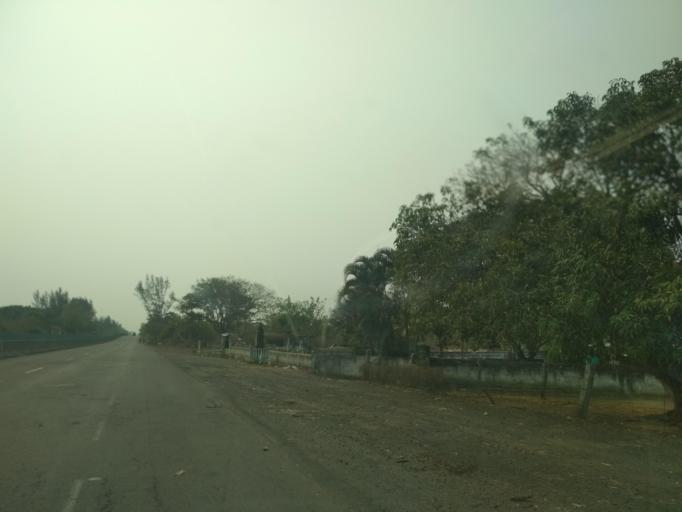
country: MX
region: Veracruz
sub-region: Veracruz
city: Las Amapolas
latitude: 19.1408
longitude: -96.2548
